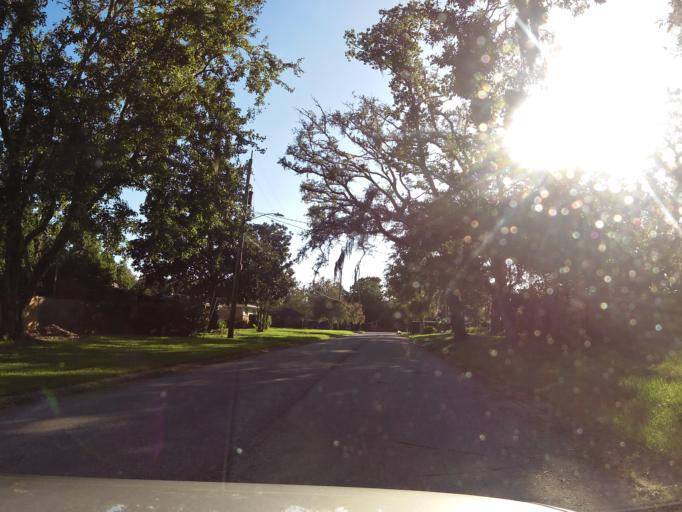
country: US
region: Florida
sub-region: Duval County
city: Jacksonville
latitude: 30.2530
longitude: -81.6297
